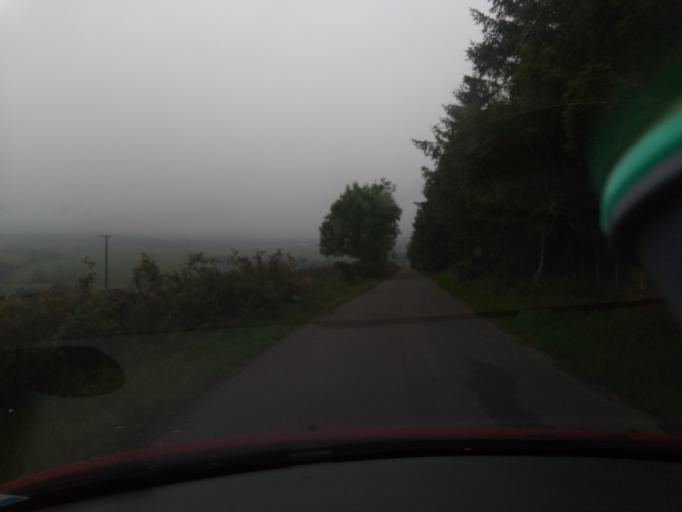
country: GB
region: Scotland
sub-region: The Scottish Borders
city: Melrose
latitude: 55.6476
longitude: -2.7580
